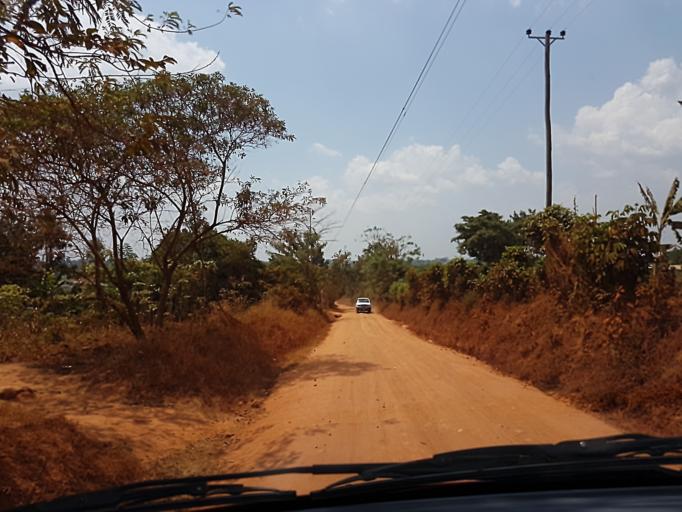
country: UG
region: Central Region
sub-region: Wakiso District
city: Bweyogerere
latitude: 0.4749
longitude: 32.6356
